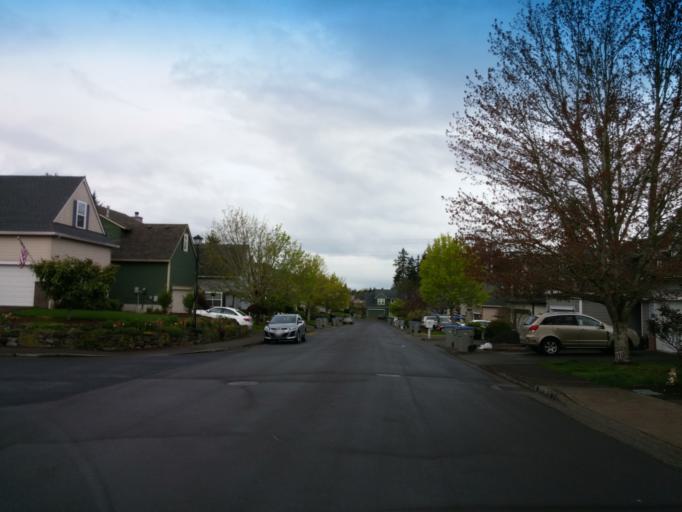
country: US
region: Oregon
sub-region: Washington County
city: Oak Hills
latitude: 45.5401
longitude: -122.8432
